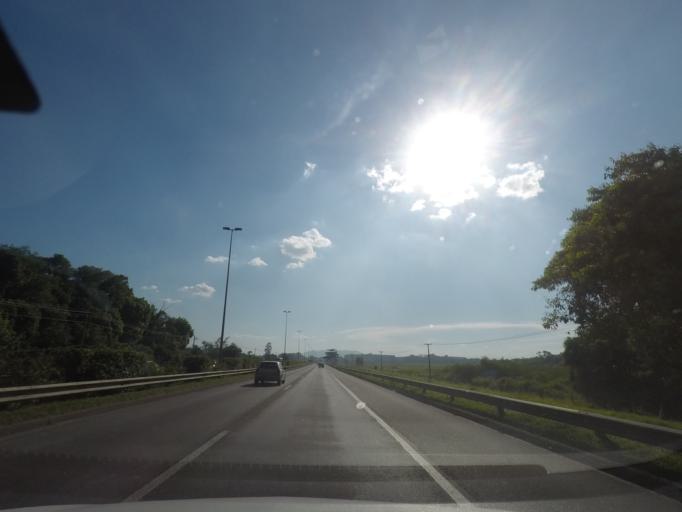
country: BR
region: Rio de Janeiro
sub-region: Duque De Caxias
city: Duque de Caxias
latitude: -22.6608
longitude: -43.2533
